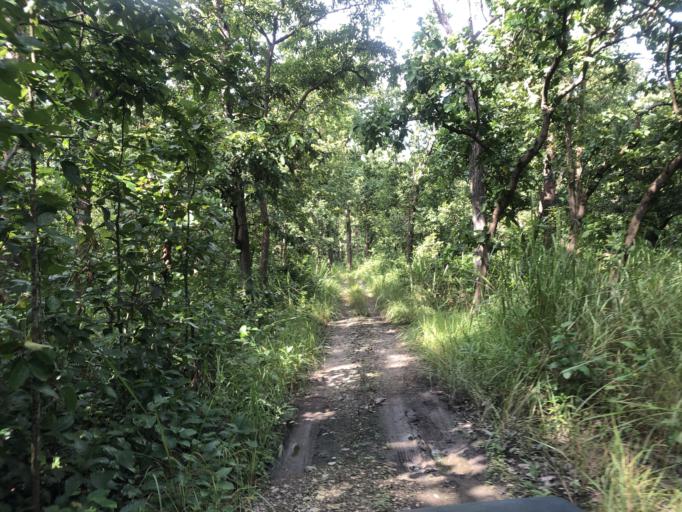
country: NP
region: Far Western
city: Tikapur
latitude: 28.5553
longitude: 81.2922
